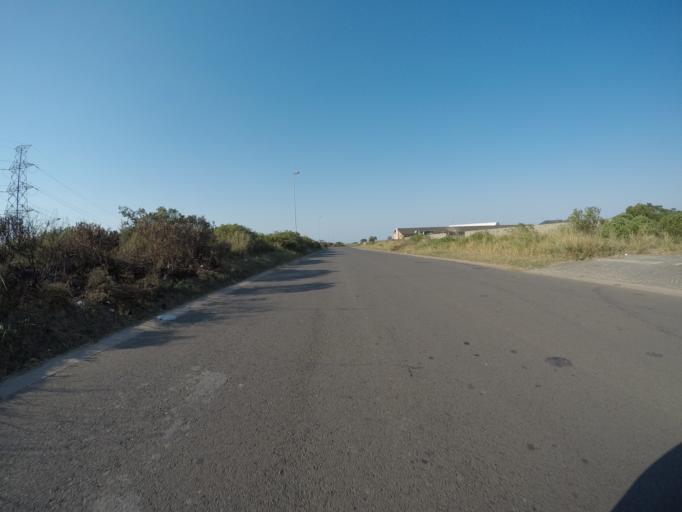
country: ZA
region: KwaZulu-Natal
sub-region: uThungulu District Municipality
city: Richards Bay
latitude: -28.7350
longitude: 32.0389
